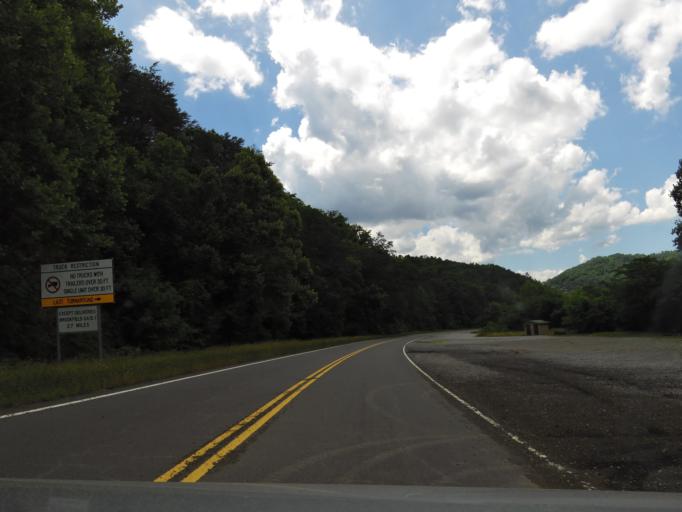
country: US
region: Tennessee
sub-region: Blount County
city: Maryville
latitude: 35.5472
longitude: -83.9914
